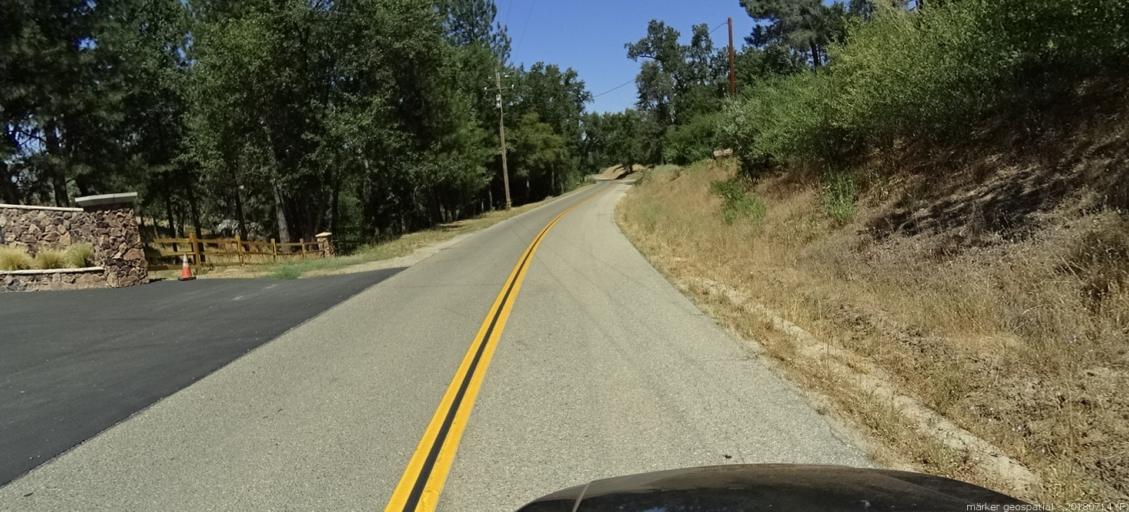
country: US
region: California
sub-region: Madera County
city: Oakhurst
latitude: 37.3705
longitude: -119.6625
